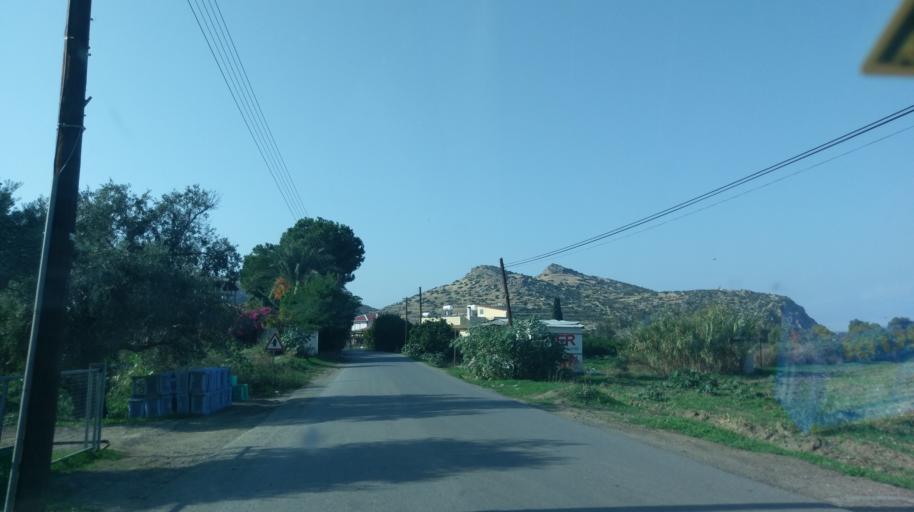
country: CY
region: Lefkosia
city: Kato Pyrgos
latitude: 35.1670
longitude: 32.7457
